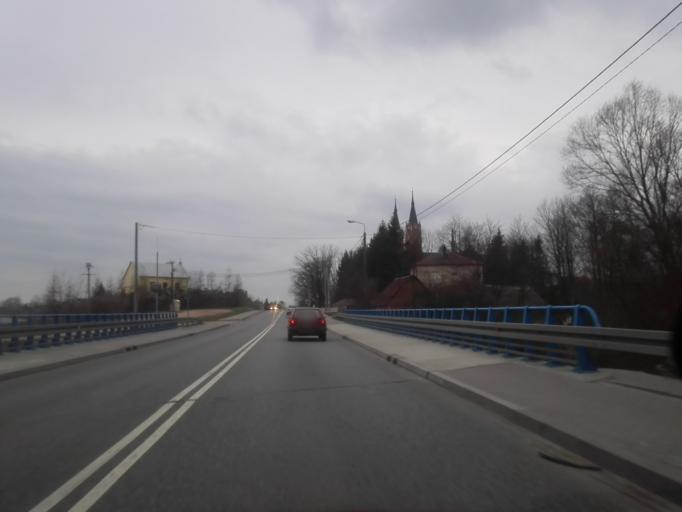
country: PL
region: Podlasie
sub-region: Powiat grajewski
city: Rajgrod
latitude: 53.7304
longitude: 22.7026
